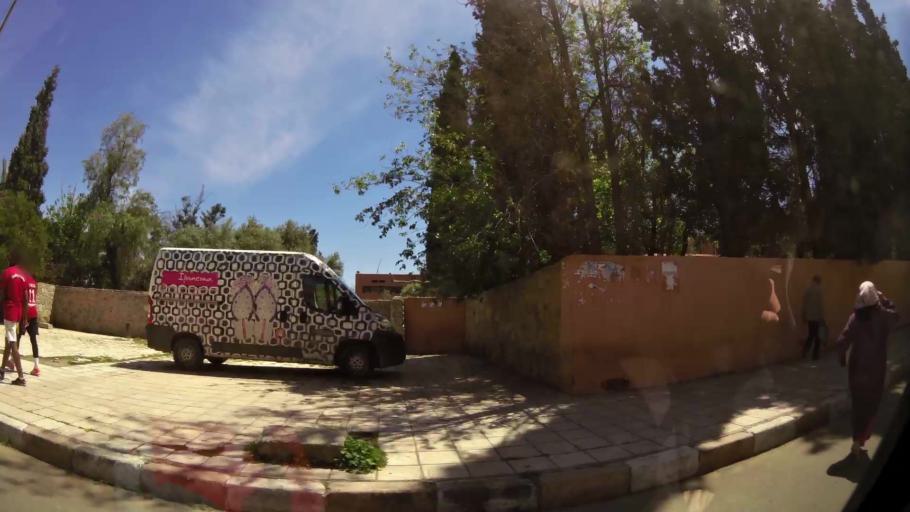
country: MA
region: Marrakech-Tensift-Al Haouz
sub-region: Marrakech
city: Marrakesh
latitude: 31.6547
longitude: -8.0022
